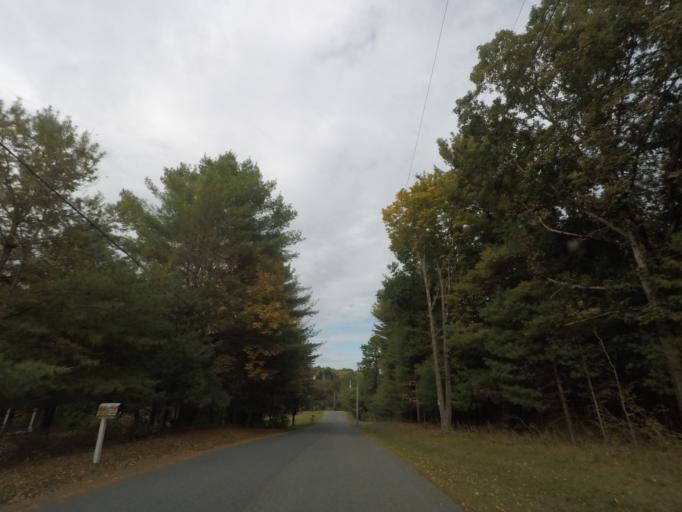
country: US
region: New York
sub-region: Rensselaer County
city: Nassau
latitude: 42.5501
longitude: -73.6428
